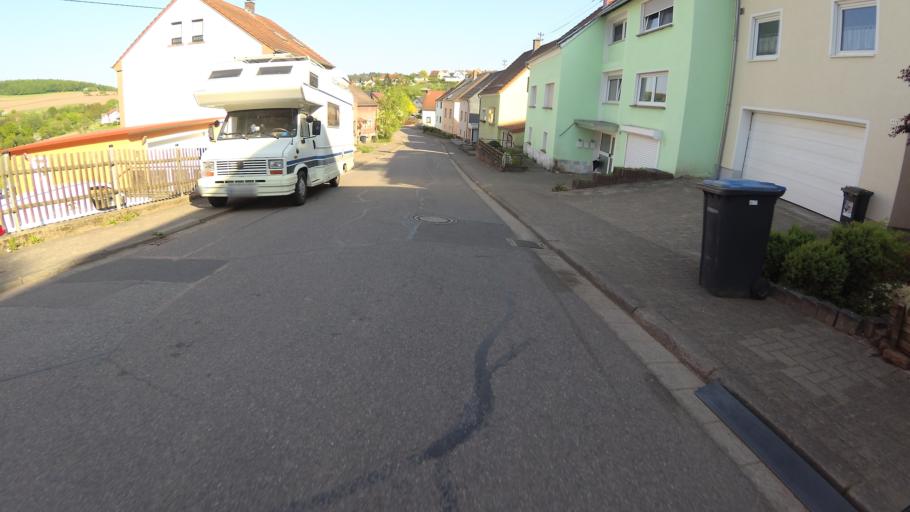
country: DE
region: Saarland
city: Illingen
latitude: 49.3992
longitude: 7.0266
